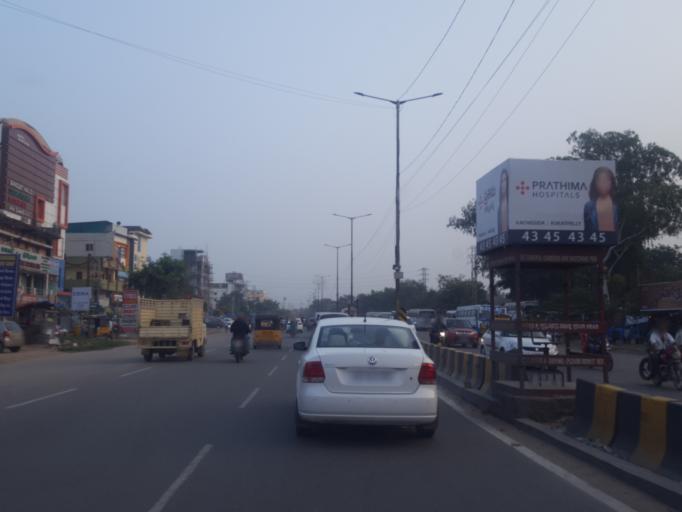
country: IN
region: Telangana
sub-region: Medak
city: Serilingampalle
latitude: 17.5019
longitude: 78.3121
